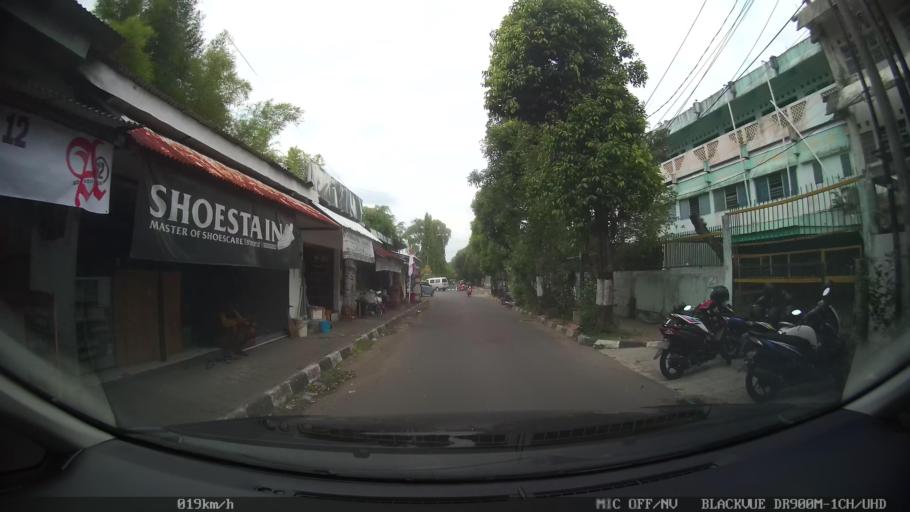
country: ID
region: Daerah Istimewa Yogyakarta
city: Yogyakarta
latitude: -7.7938
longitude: 110.3836
